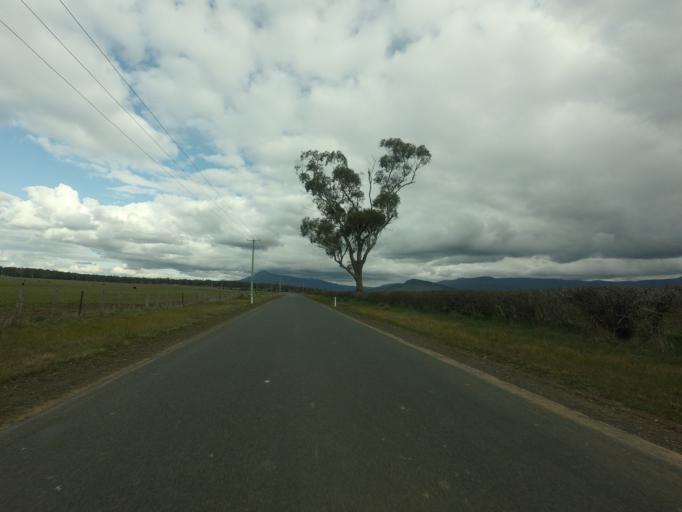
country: AU
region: Tasmania
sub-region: Northern Midlands
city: Longford
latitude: -41.7918
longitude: 147.1132
